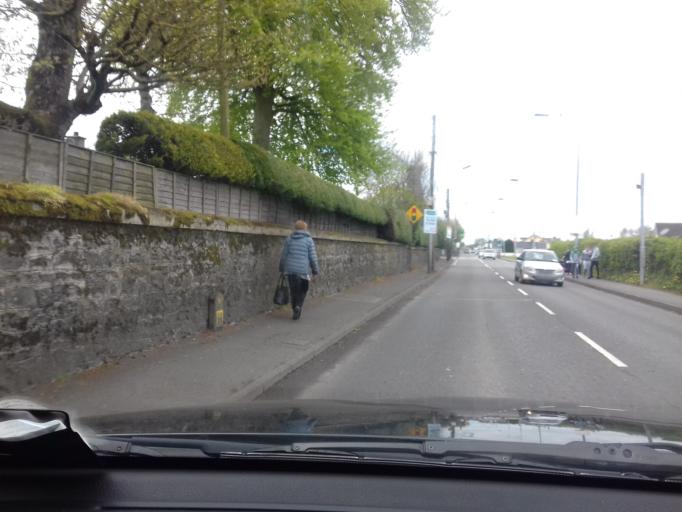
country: IE
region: Leinster
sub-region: Laois
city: Portlaoise
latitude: 53.0385
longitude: -7.3068
